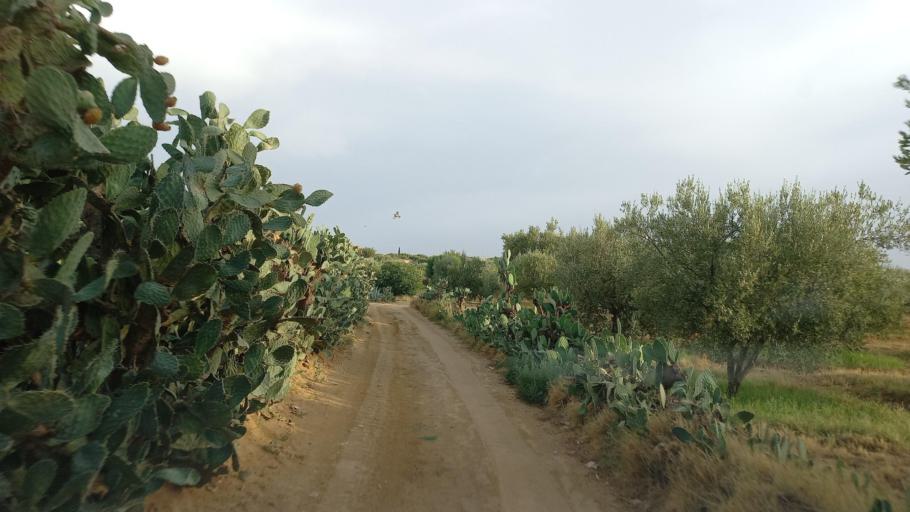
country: TN
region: Al Qasrayn
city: Kasserine
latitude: 35.2195
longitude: 9.0523
